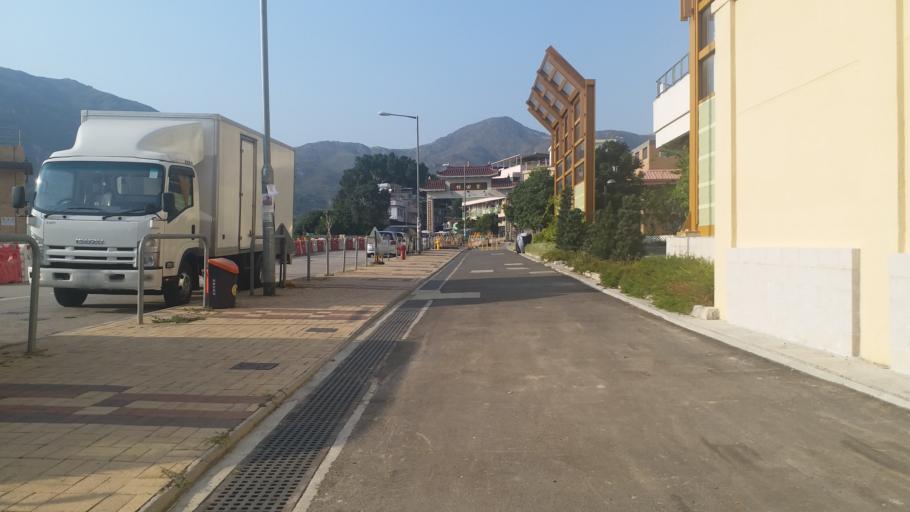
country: HK
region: Tuen Mun
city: Tuen Mun
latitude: 22.4142
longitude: 113.9750
